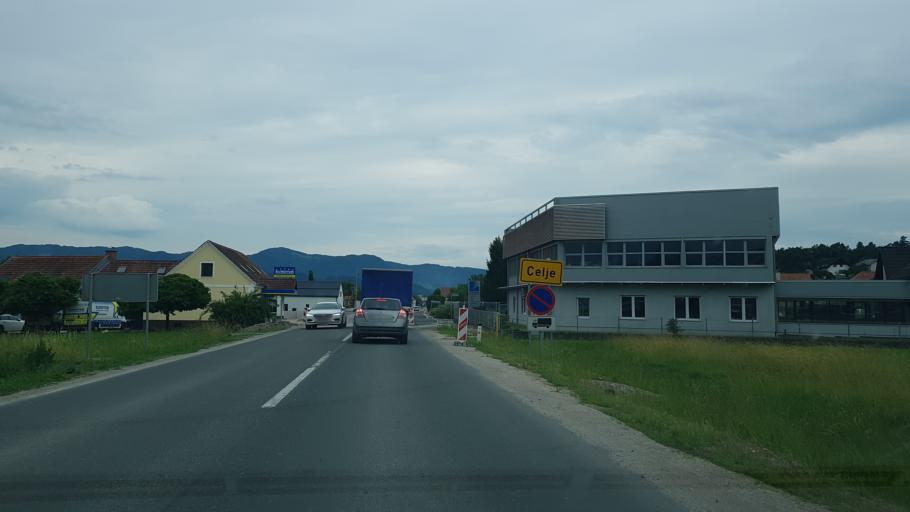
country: SI
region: Celje
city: Trnovlje pri Celju
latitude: 46.2648
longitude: 15.2835
